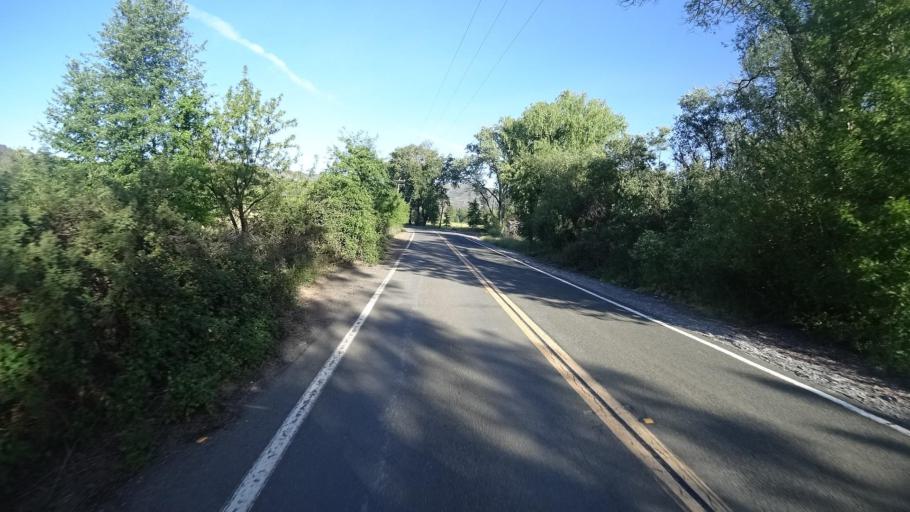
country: US
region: California
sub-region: Lake County
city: North Lakeport
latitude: 39.0943
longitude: -122.9616
